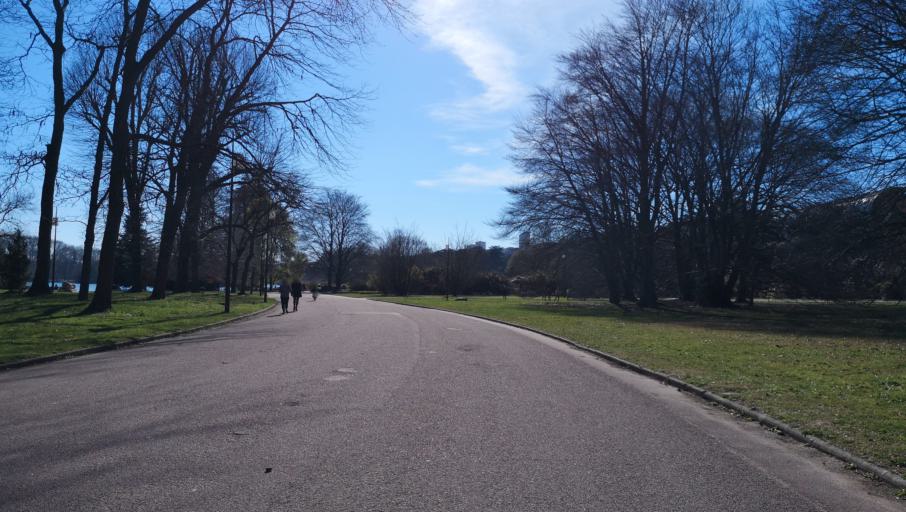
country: FR
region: Rhone-Alpes
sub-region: Departement du Rhone
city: Caluire-et-Cuire
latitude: 45.7841
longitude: 4.8554
